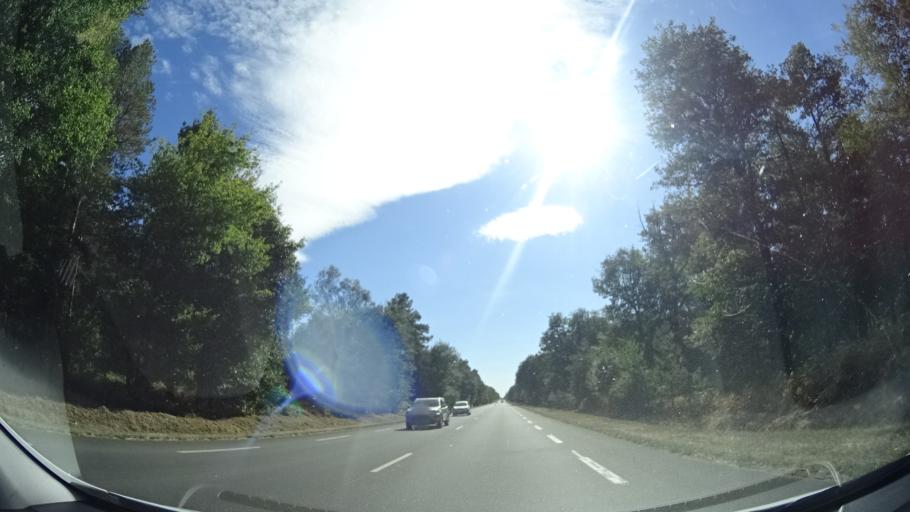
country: FR
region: Centre
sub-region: Departement du Loiret
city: Vitry-aux-Loges
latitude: 47.9239
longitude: 2.3268
